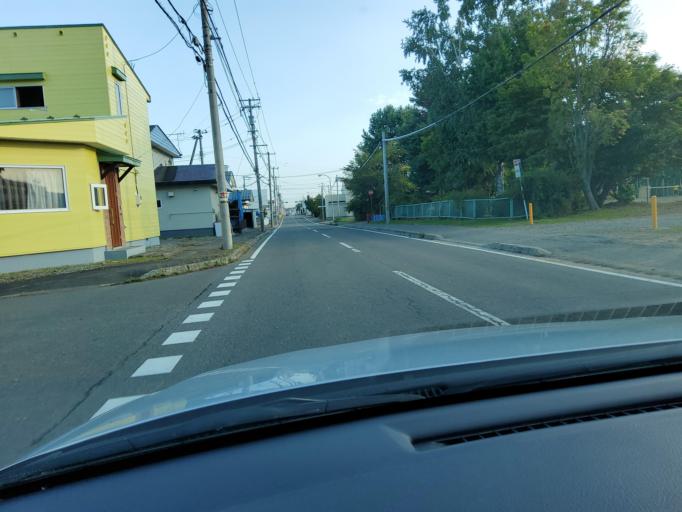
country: JP
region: Hokkaido
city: Obihiro
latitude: 42.9397
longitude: 143.1825
